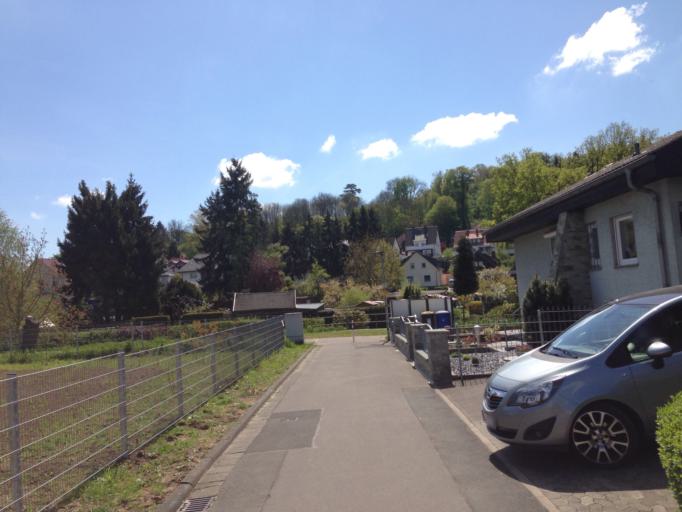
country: DE
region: Hesse
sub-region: Regierungsbezirk Giessen
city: Lich
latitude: 50.5163
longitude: 8.8121
